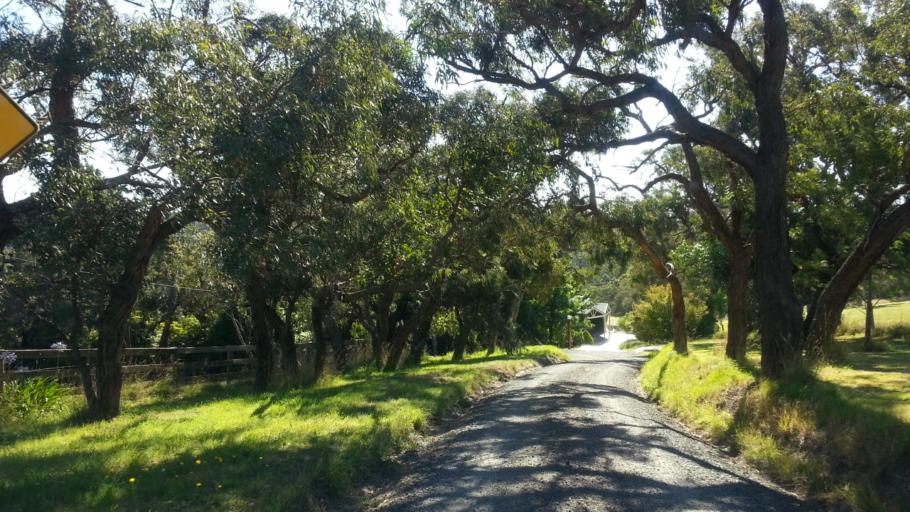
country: AU
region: Victoria
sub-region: Yarra Ranges
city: Selby
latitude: -37.9551
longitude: 145.3704
